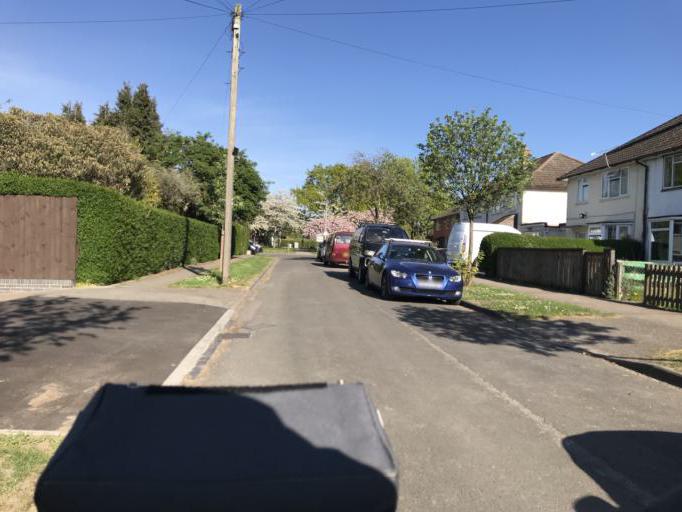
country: GB
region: England
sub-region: Cambridgeshire
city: Cambridge
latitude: 52.2114
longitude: 0.1615
